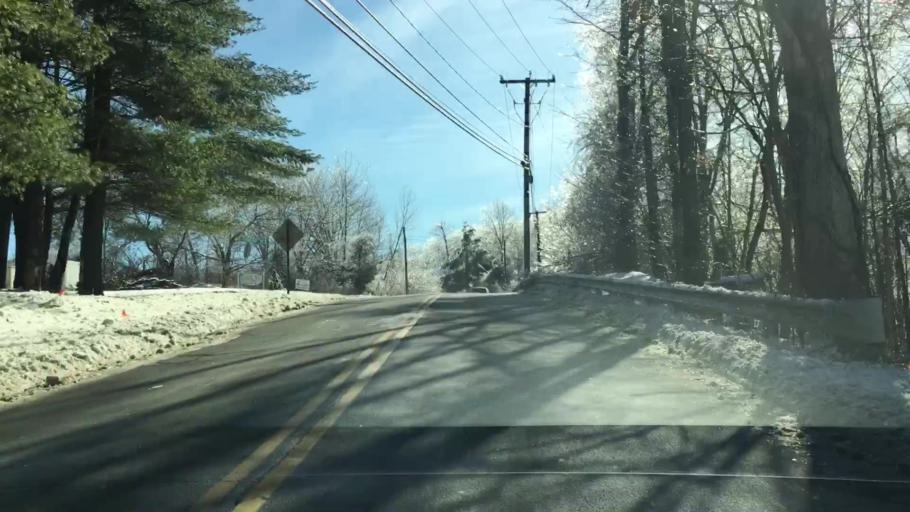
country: US
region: Connecticut
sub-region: Fairfield County
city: Newtown
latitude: 41.4063
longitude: -73.2633
